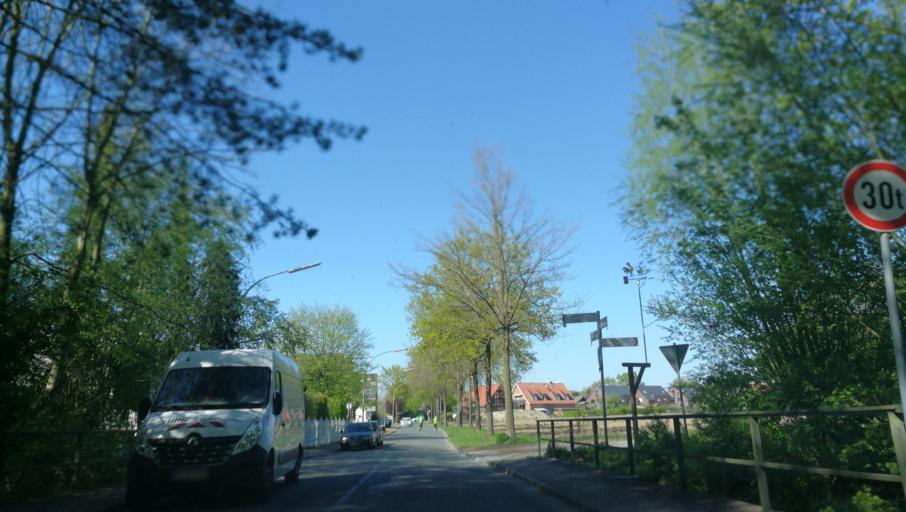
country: DE
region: North Rhine-Westphalia
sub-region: Regierungsbezirk Munster
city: Muenster
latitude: 51.9454
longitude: 7.5377
